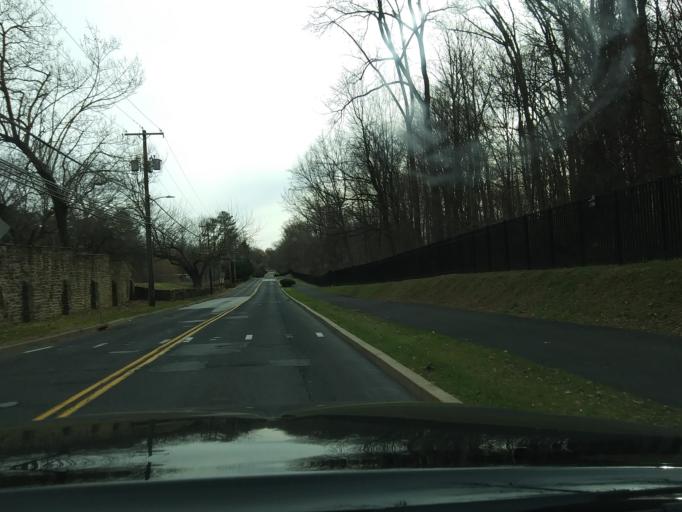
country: US
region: Pennsylvania
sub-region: Montgomery County
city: Jenkintown
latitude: 40.0929
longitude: -75.1112
